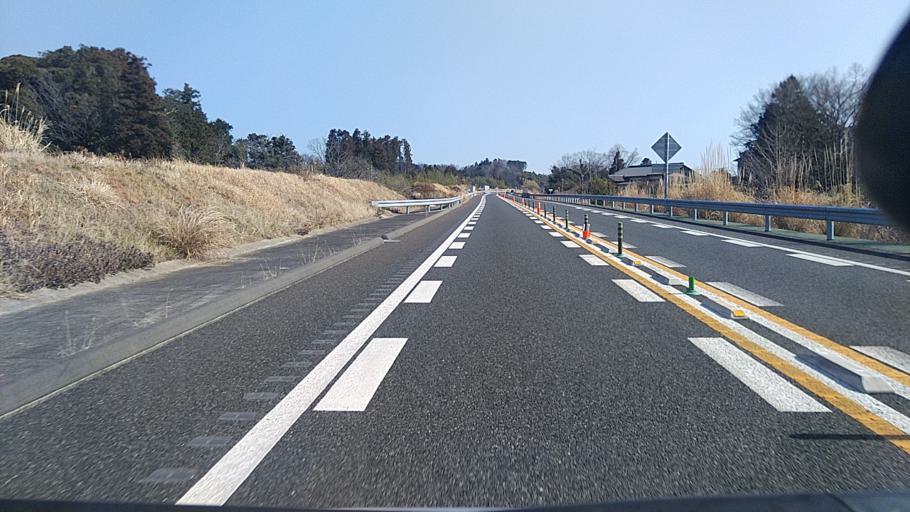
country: JP
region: Chiba
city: Mobara
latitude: 35.3603
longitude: 140.1517
